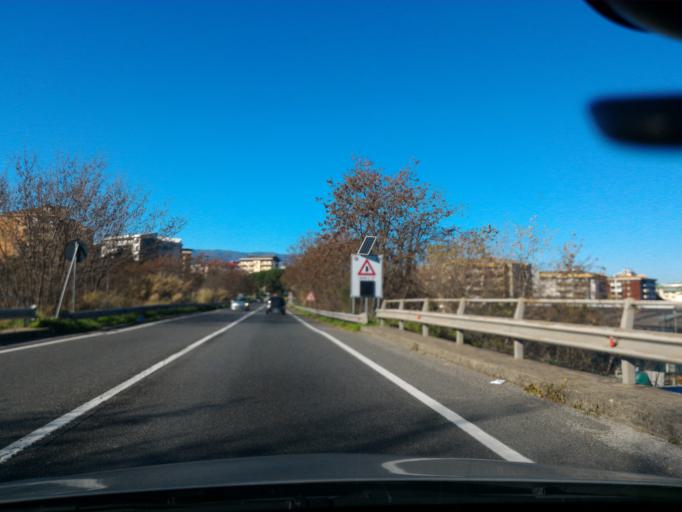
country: IT
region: Calabria
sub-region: Provincia di Cosenza
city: Quattromiglia
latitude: 39.3291
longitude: 16.2493
